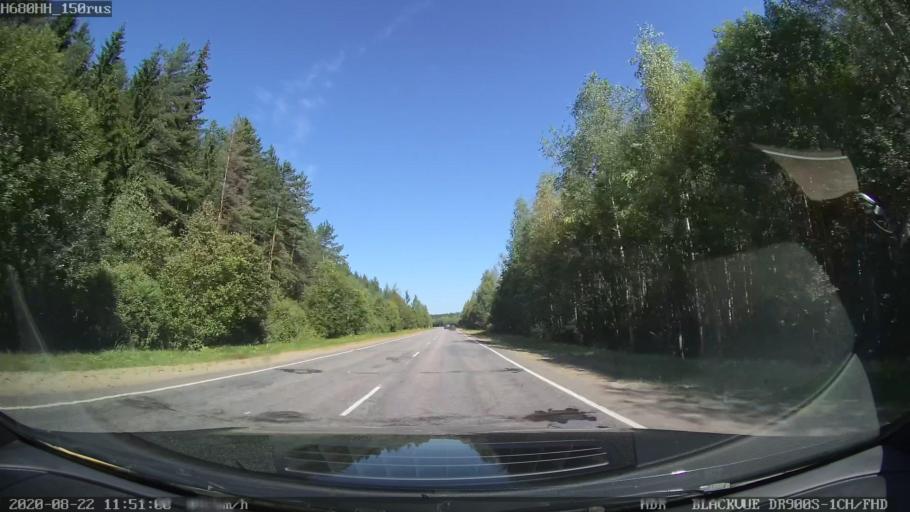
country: RU
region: Tverskaya
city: Sakharovo
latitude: 57.0986
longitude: 36.1190
